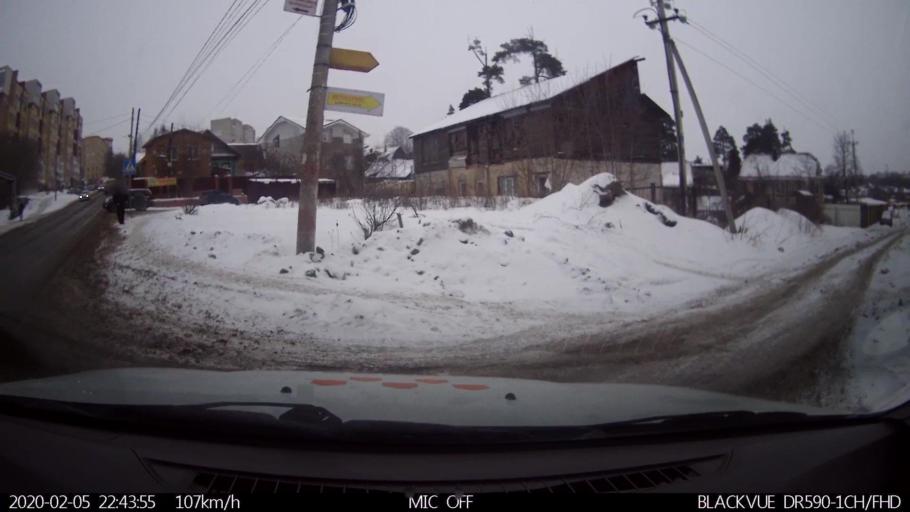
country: RU
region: Nizjnij Novgorod
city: Imeni Stepana Razina
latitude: 54.7099
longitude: 44.3961
